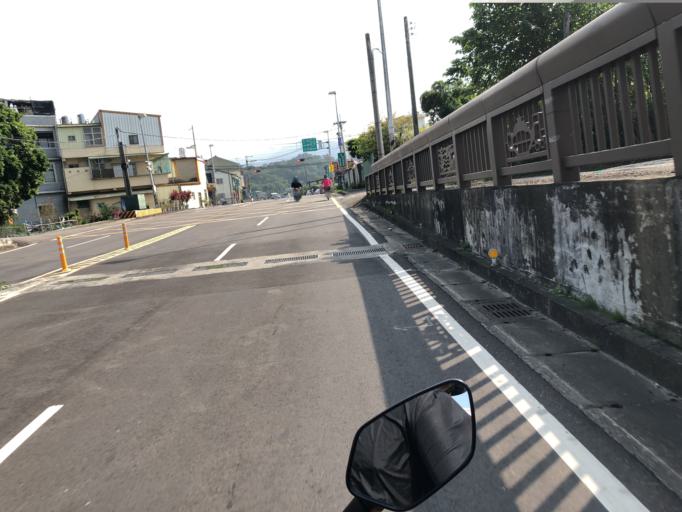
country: TW
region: Taiwan
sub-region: Miaoli
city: Miaoli
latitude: 24.5441
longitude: 120.8352
